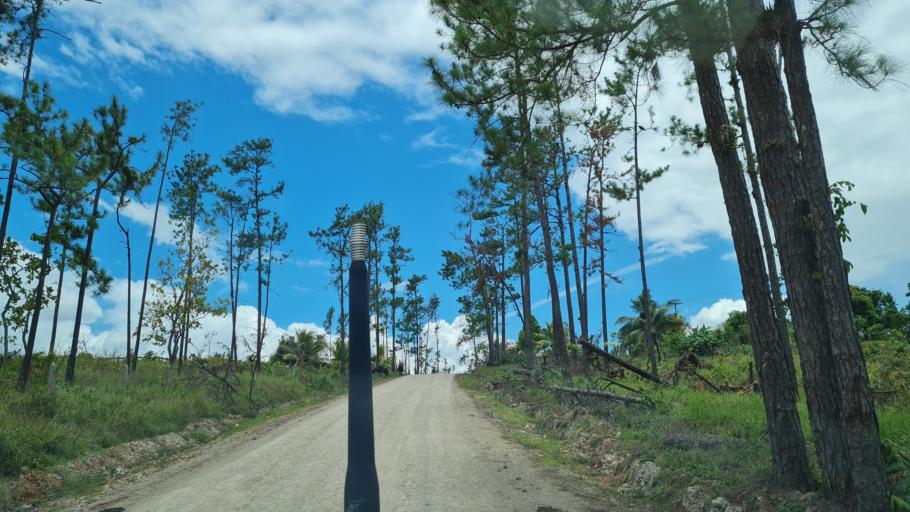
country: NI
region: Atlantico Sur
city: La Cruz de Rio Grande
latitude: 13.5735
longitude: -84.3227
